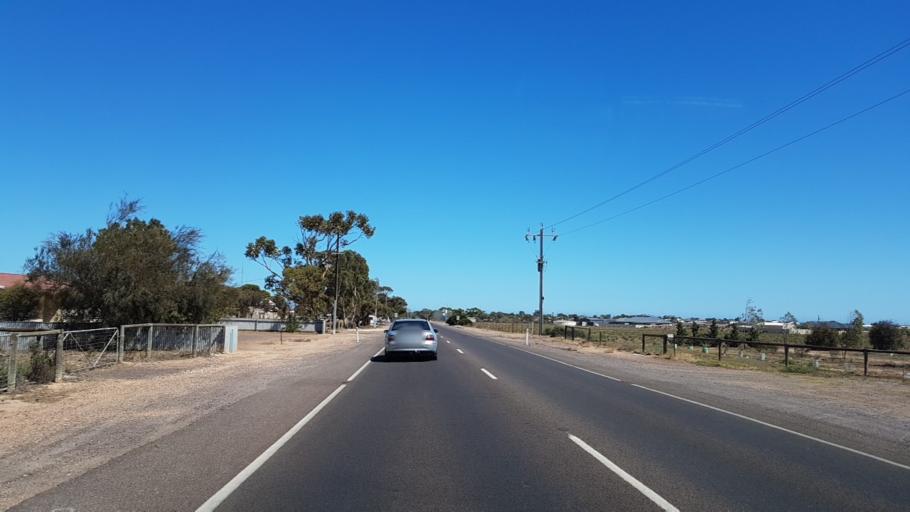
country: AU
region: South Australia
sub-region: Copper Coast
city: Wallaroo
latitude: -33.9397
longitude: 137.6499
